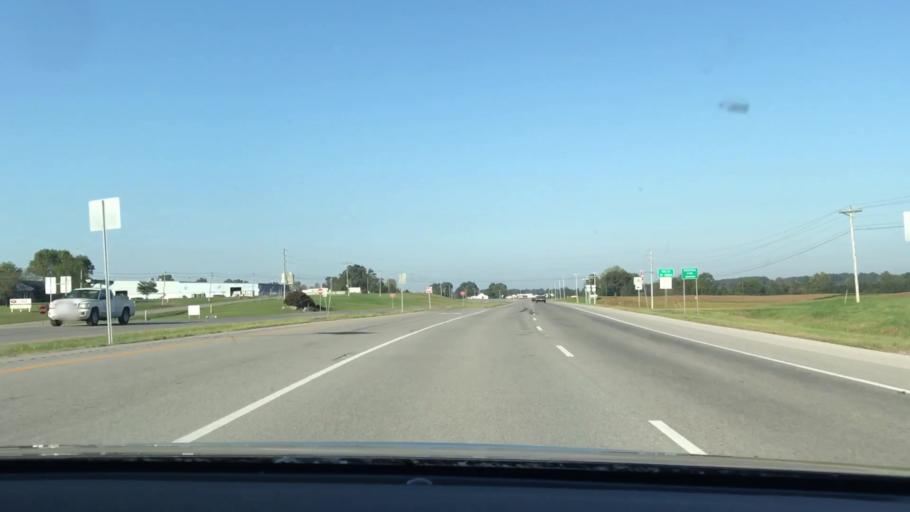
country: US
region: Kentucky
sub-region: Trigg County
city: Cadiz
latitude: 36.8770
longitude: -87.7432
